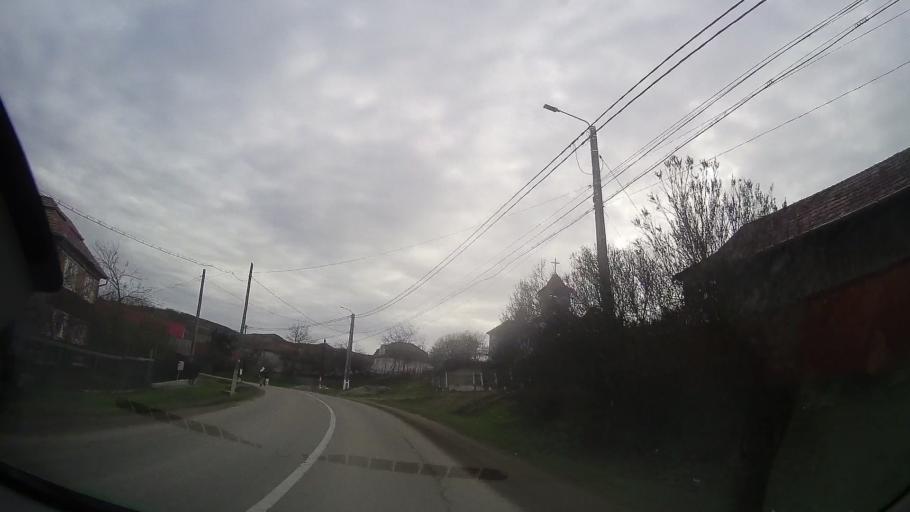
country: RO
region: Bistrita-Nasaud
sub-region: Comuna Budesti
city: Budesti
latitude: 46.8755
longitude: 24.2435
